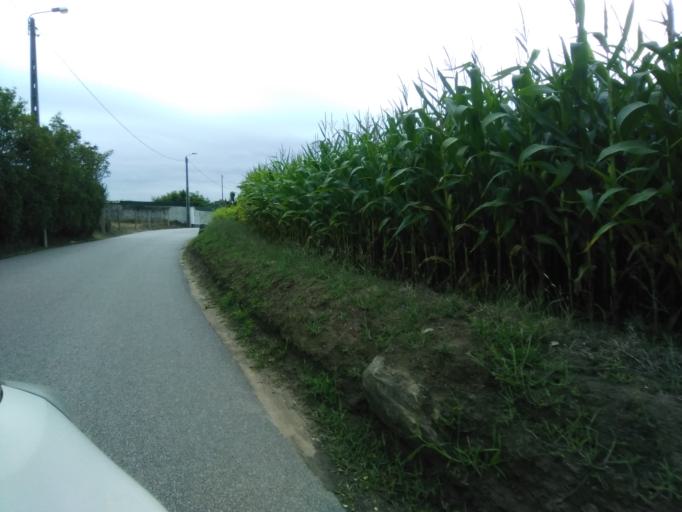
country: PT
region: Porto
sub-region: Matosinhos
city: Lavra
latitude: 41.2438
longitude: -8.7131
